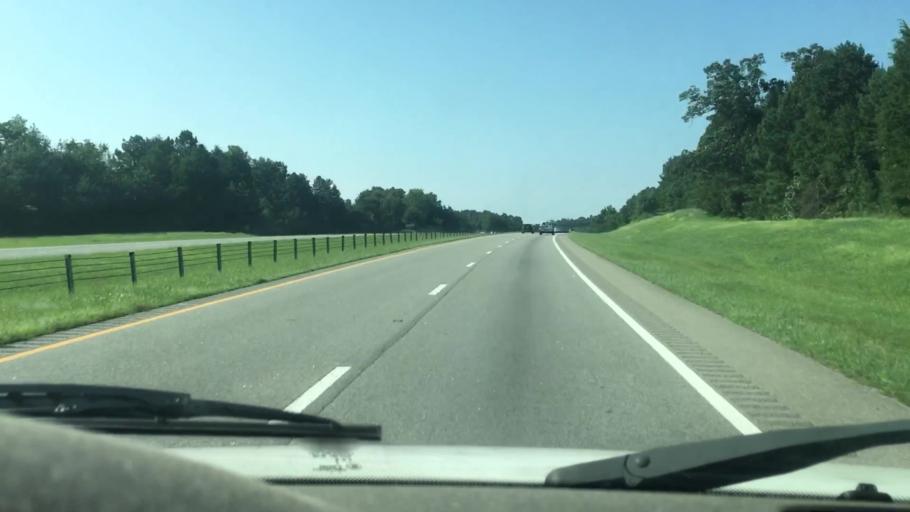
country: US
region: North Carolina
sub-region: Lincoln County
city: Lowesville
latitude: 35.3929
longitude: -80.9985
